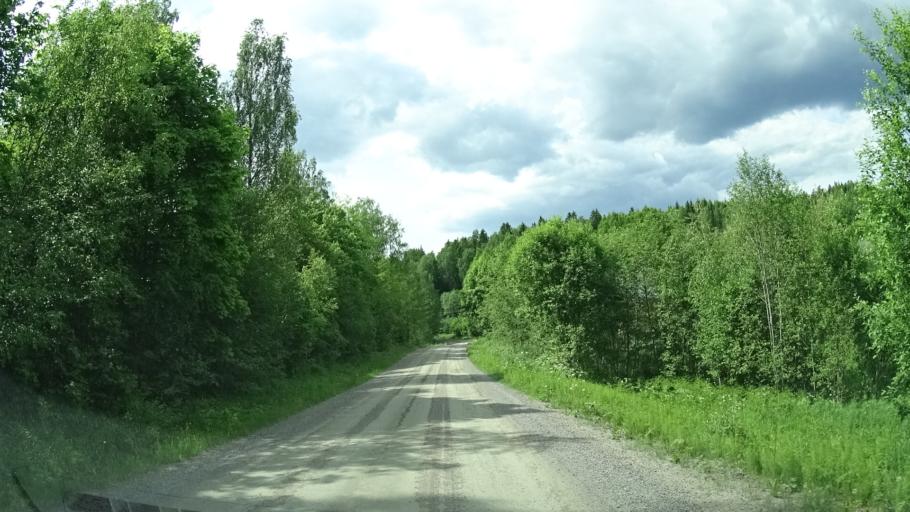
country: FI
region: Uusimaa
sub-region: Helsinki
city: Siuntio
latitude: 60.2132
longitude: 24.2763
